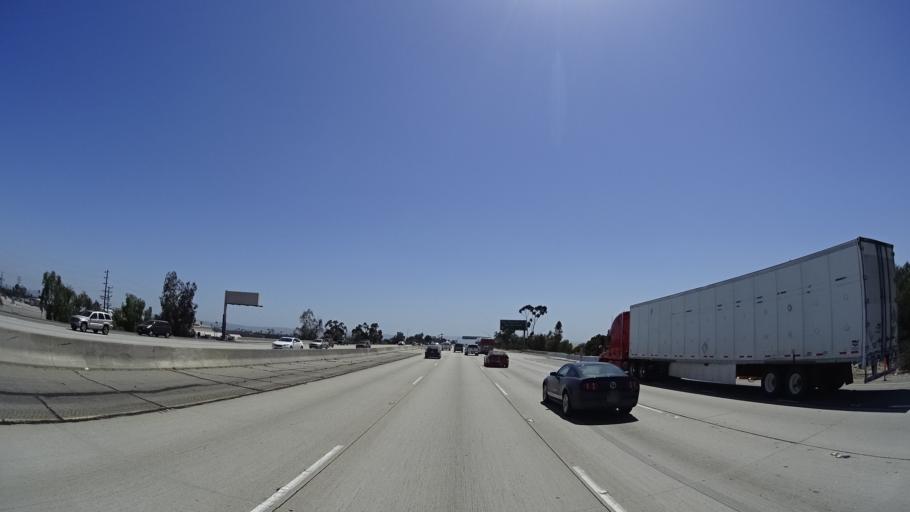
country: US
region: California
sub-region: Los Angeles County
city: San Fernando
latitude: 34.2761
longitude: -118.4243
